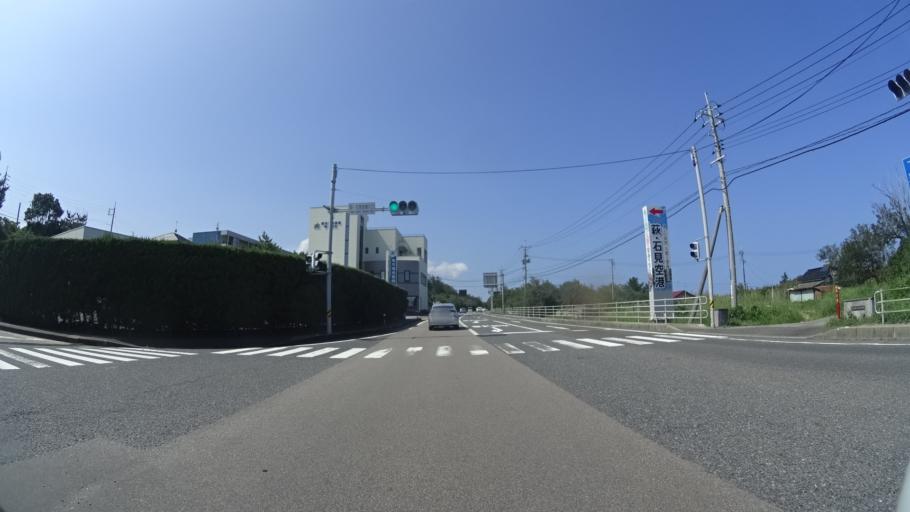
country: JP
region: Shimane
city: Masuda
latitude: 34.6887
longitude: 131.8051
